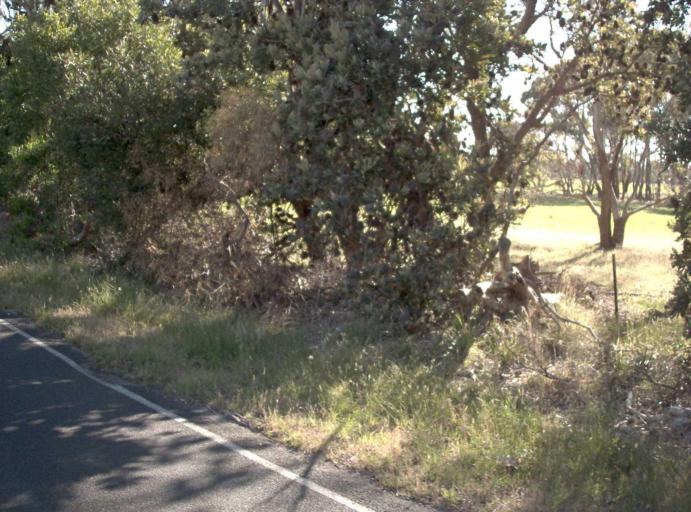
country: AU
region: Victoria
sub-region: Latrobe
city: Morwell
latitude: -38.6983
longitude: 146.3993
